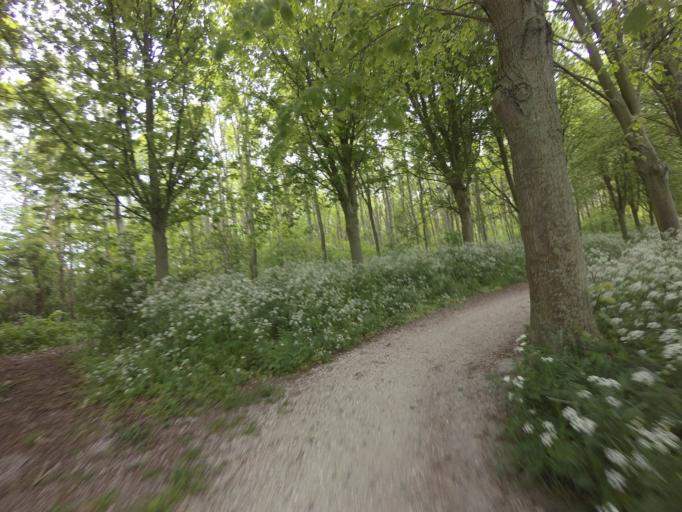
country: NL
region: Friesland
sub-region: Sudwest Fryslan
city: Bolsward
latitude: 53.0967
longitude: 5.4725
